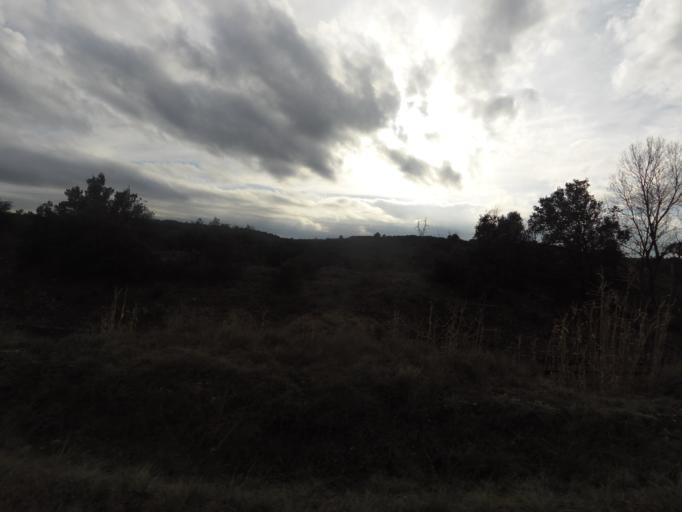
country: FR
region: Languedoc-Roussillon
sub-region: Departement du Gard
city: La Calmette
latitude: 43.8900
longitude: 4.2366
